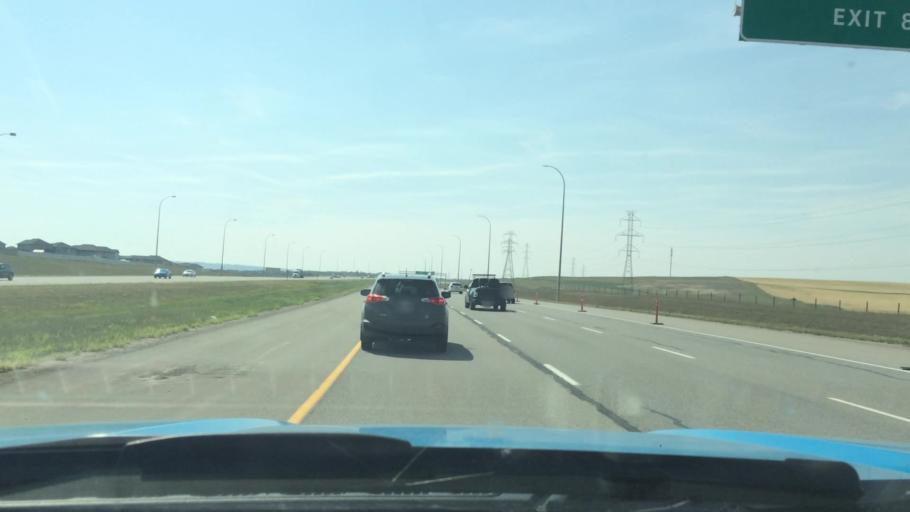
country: CA
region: Alberta
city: Airdrie
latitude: 51.1752
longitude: -114.0504
